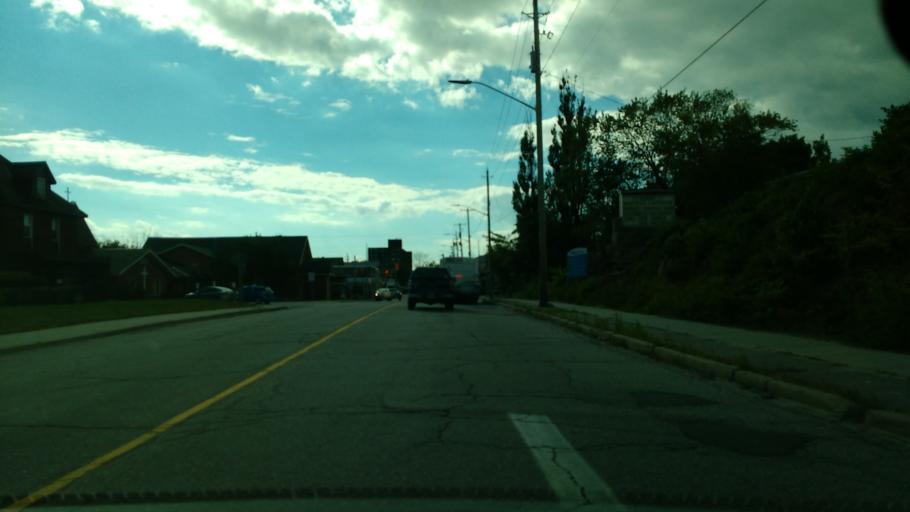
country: CA
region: Ontario
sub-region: Nipissing District
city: North Bay
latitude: 46.3180
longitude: -79.4532
